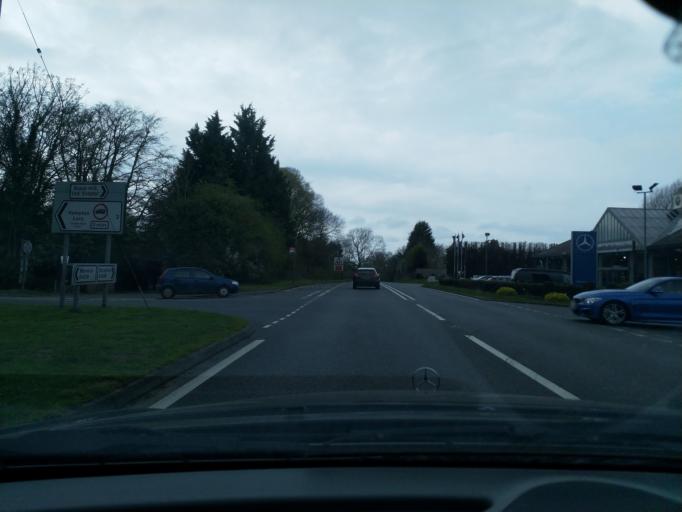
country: GB
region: England
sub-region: Warwickshire
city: Stratford-upon-Avon
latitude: 52.2312
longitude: -1.6583
